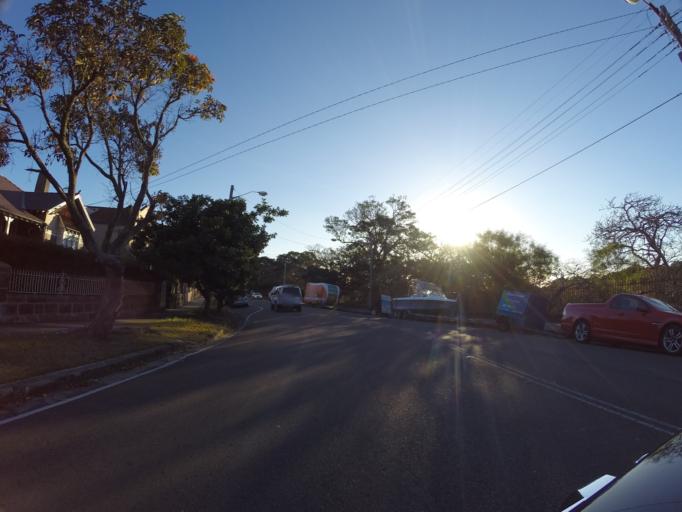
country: AU
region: New South Wales
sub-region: Waverley
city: Bondi Junction
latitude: -33.9026
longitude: 151.2430
